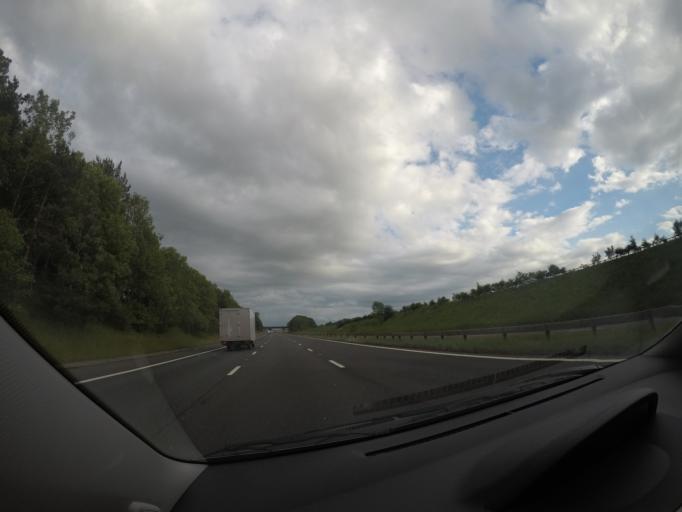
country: GB
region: England
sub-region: Cumbria
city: Penrith
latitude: 54.7183
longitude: -2.7981
